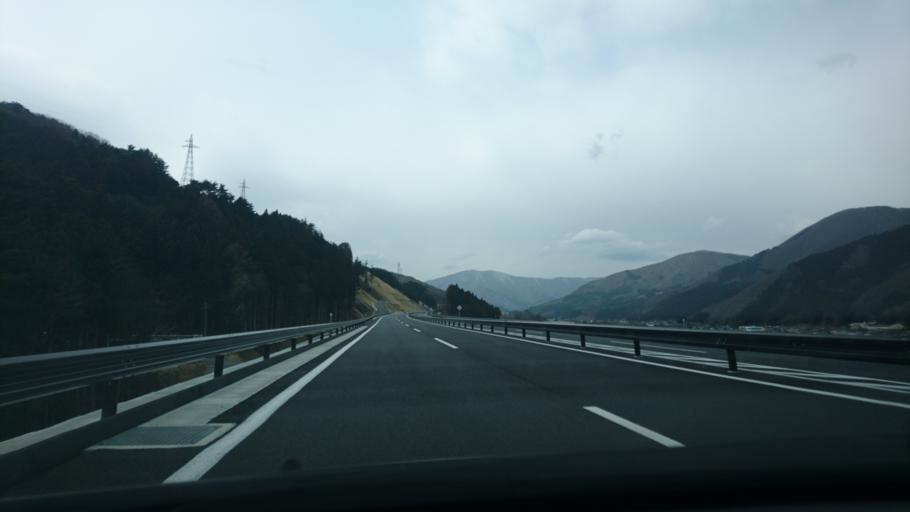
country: JP
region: Iwate
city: Kamaishi
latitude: 39.2518
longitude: 141.8070
